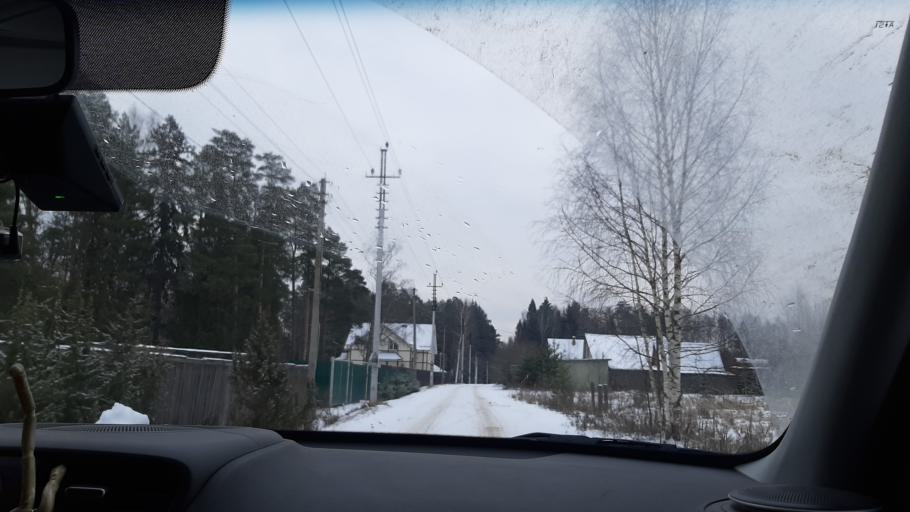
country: RU
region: Ivanovo
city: Kokhma
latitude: 56.9008
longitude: 41.0081
